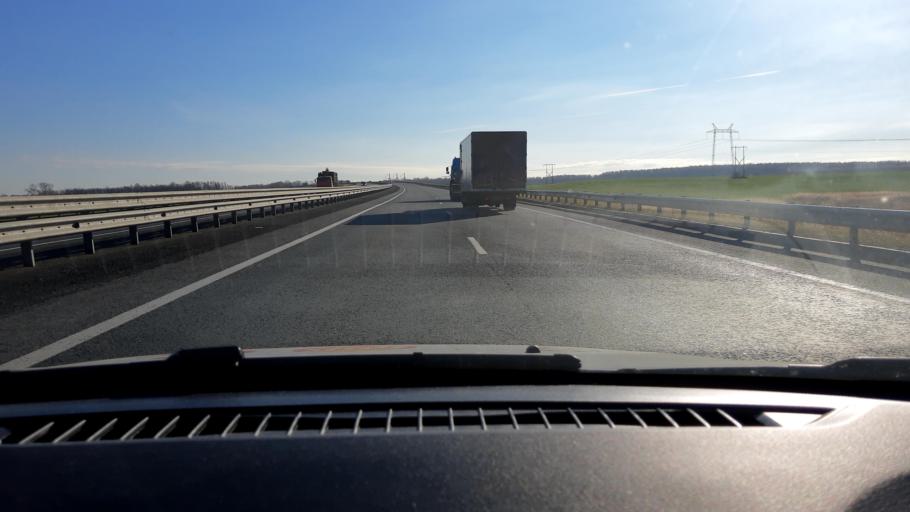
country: RU
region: Nizjnij Novgorod
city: Burevestnik
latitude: 56.1182
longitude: 43.8185
